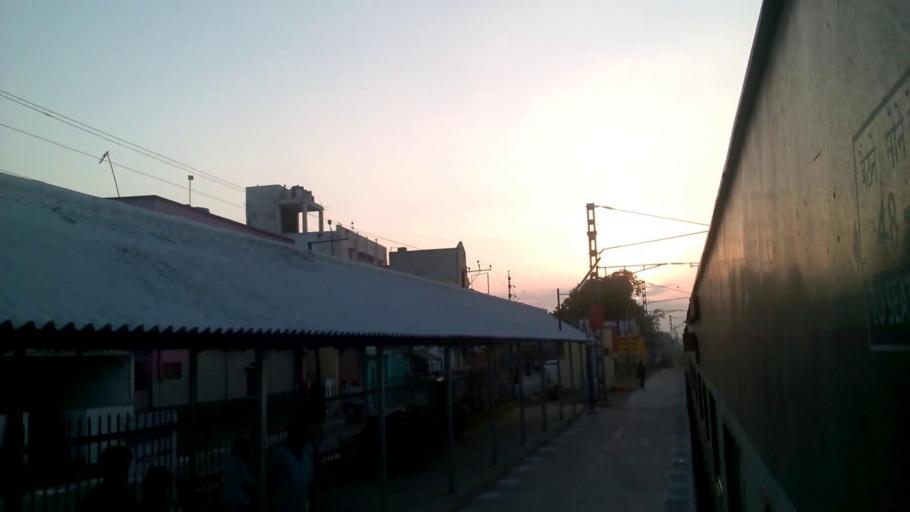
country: IN
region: Tamil Nadu
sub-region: Thoothukkudi
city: Korampallam
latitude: 8.8083
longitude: 78.1457
